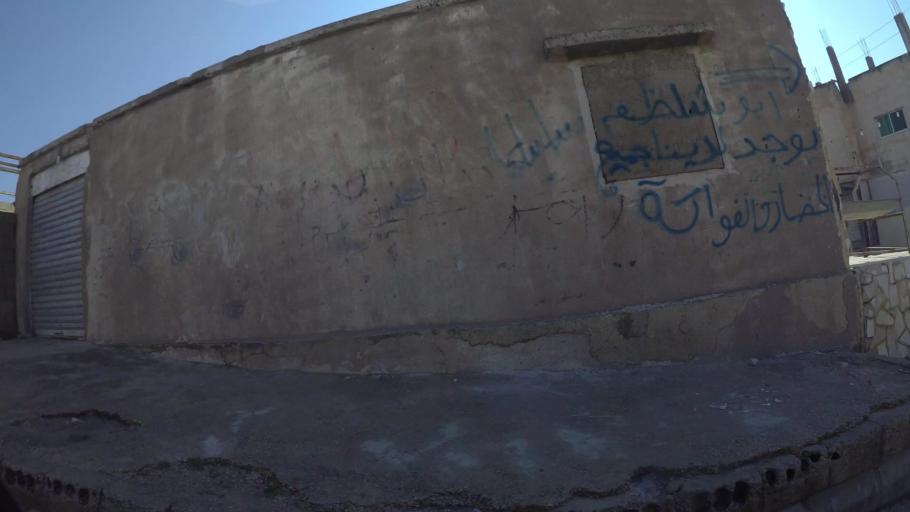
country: JO
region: Amman
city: Al Jubayhah
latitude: 32.0684
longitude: 35.8449
